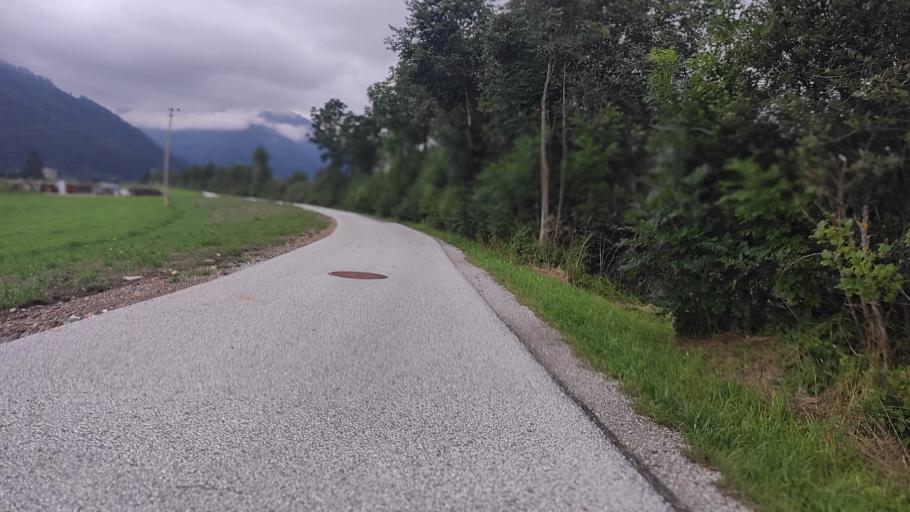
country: AT
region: Salzburg
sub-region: Politischer Bezirk Zell am See
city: Mittersill
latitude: 47.2834
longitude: 12.4549
